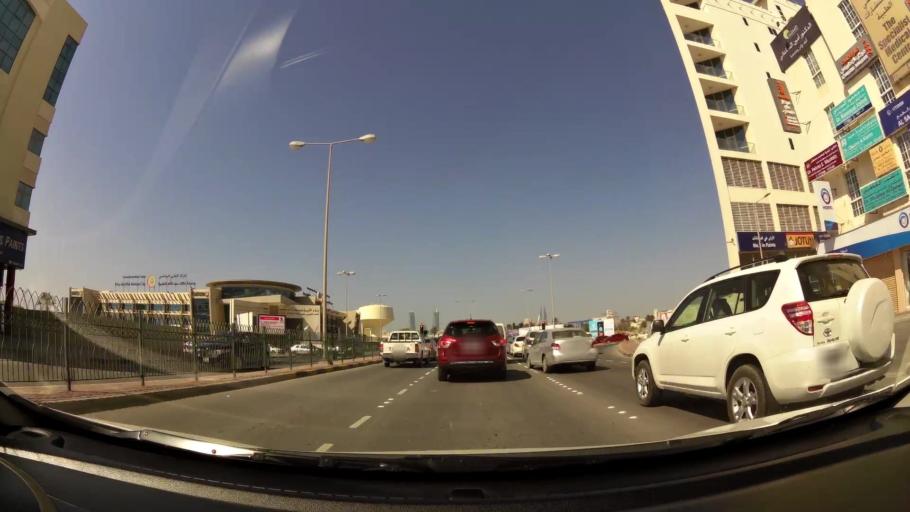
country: BH
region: Manama
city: Manama
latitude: 26.2117
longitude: 50.5756
